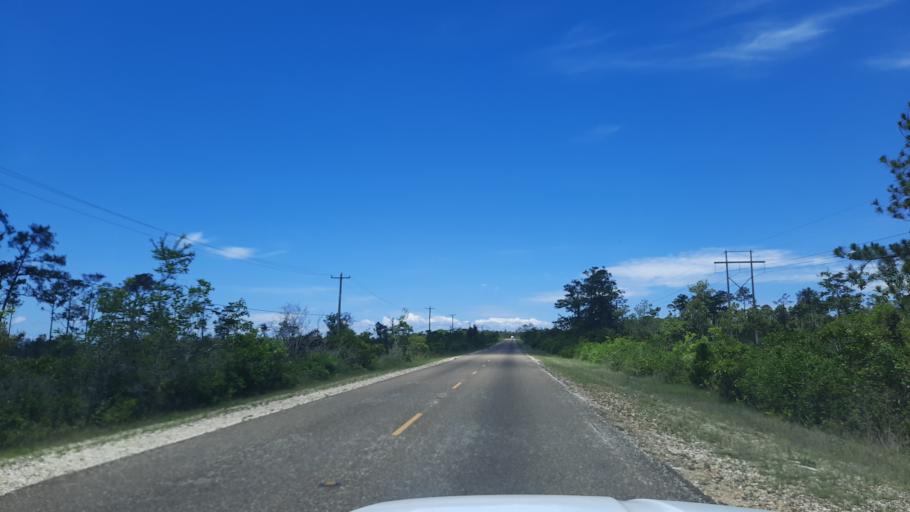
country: BZ
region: Cayo
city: Belmopan
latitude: 17.3597
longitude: -88.5460
